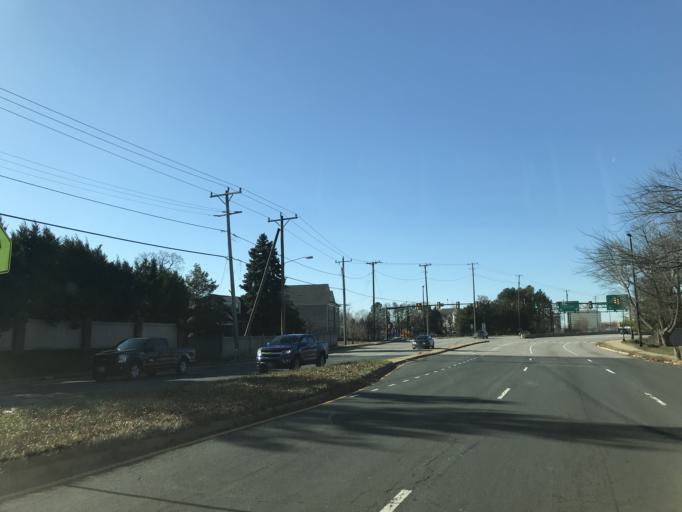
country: US
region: Virginia
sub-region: Fairfax County
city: Franconia
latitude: 38.7782
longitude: -77.1674
